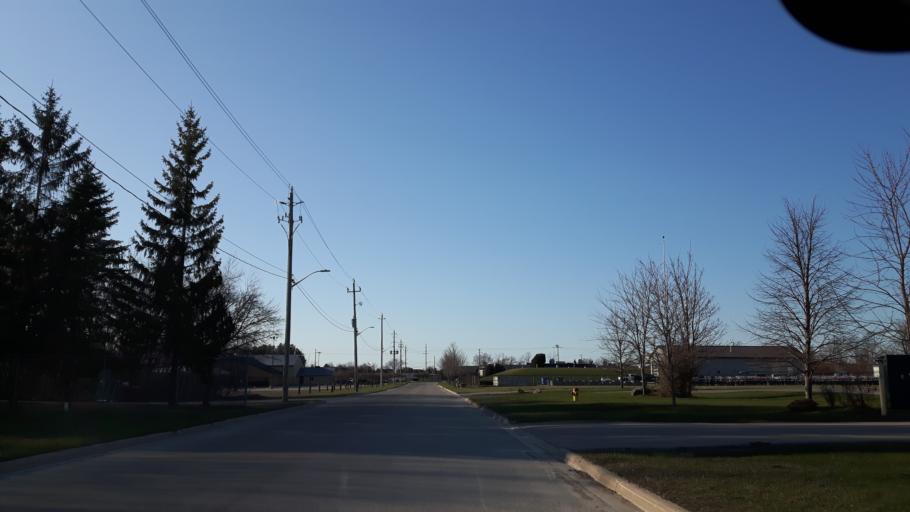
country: CA
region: Ontario
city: Goderich
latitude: 43.7289
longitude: -81.6939
